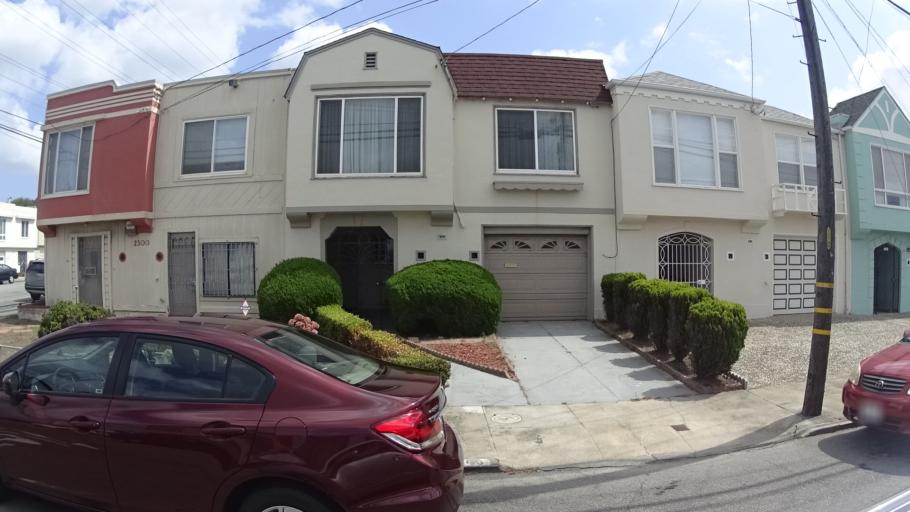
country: US
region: California
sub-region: San Mateo County
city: Daly City
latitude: 37.7437
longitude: -122.4972
